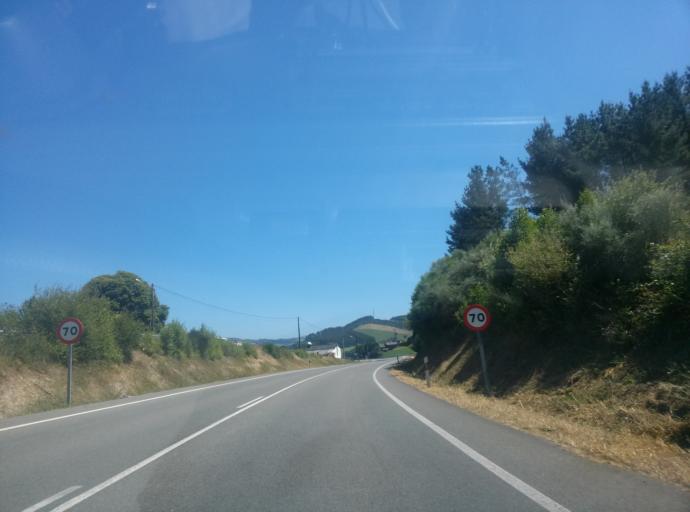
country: ES
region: Galicia
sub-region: Provincia de Lugo
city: Meira
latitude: 43.2278
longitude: -7.3309
